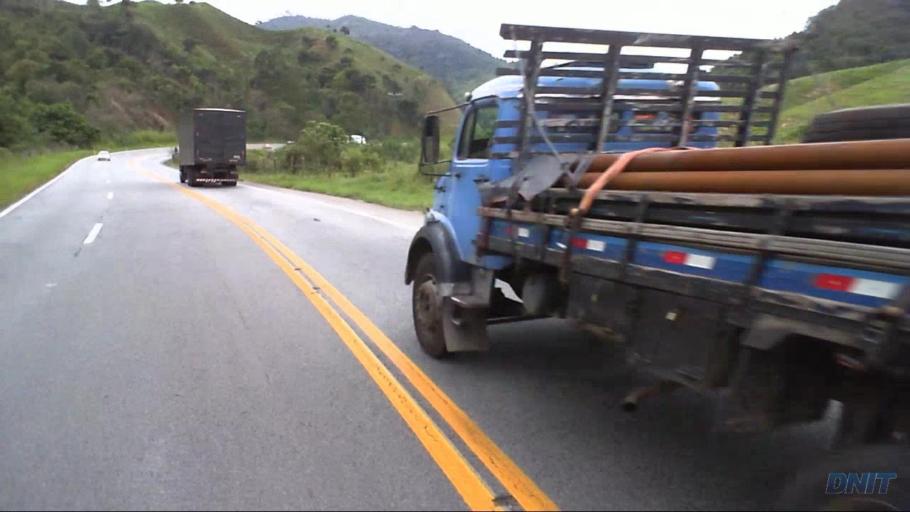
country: BR
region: Minas Gerais
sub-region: Nova Era
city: Nova Era
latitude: -19.6299
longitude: -42.8737
